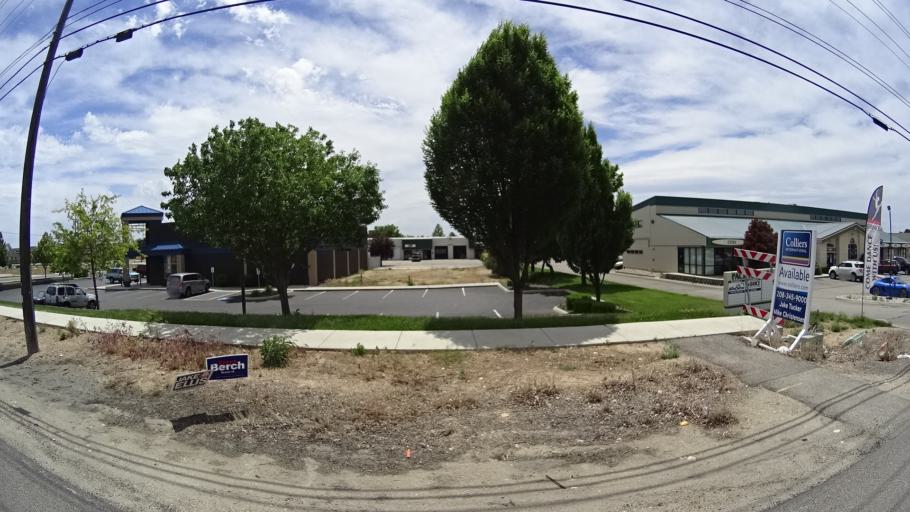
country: US
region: Idaho
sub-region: Ada County
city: Meridian
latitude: 43.6194
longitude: -116.3252
